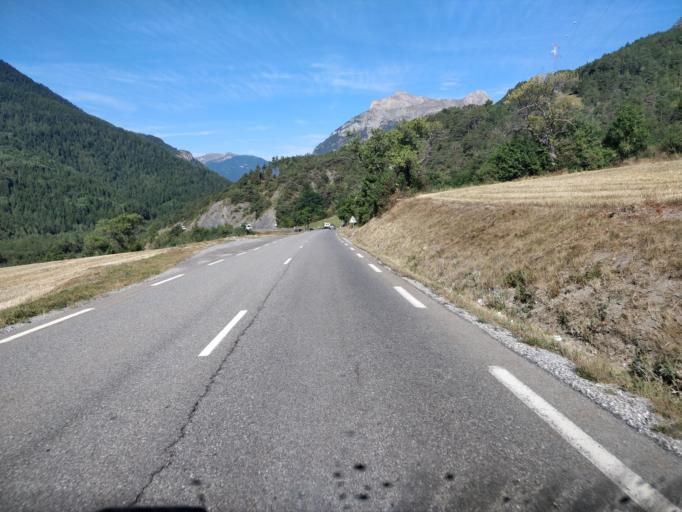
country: FR
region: Provence-Alpes-Cote d'Azur
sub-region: Departement des Alpes-de-Haute-Provence
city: Barcelonnette
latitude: 44.3931
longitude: 6.5613
